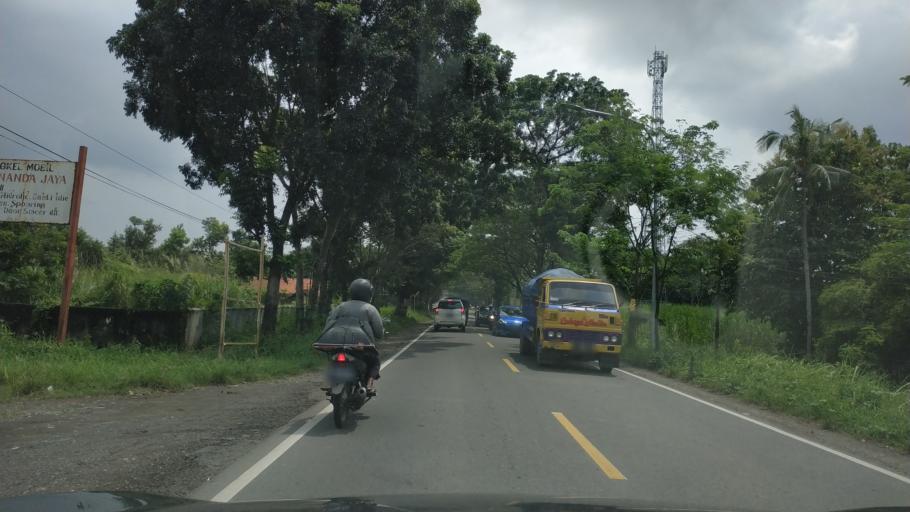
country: ID
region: Central Java
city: Slawi
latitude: -7.0104
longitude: 109.1412
